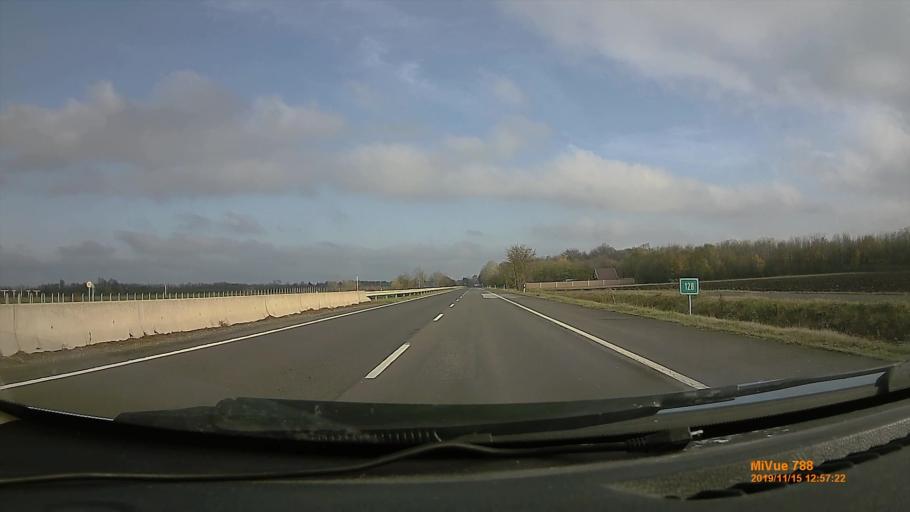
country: HU
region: Bekes
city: Bekescsaba
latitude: 46.6734
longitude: 21.1615
